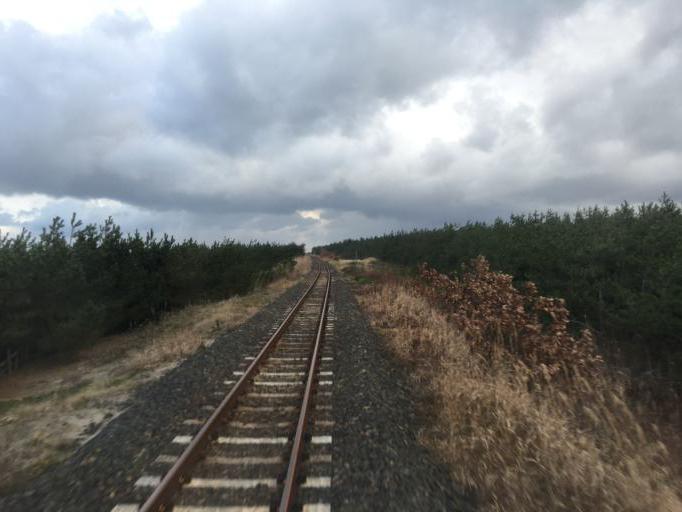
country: JP
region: Aomori
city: Mutsu
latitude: 40.9849
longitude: 141.2273
